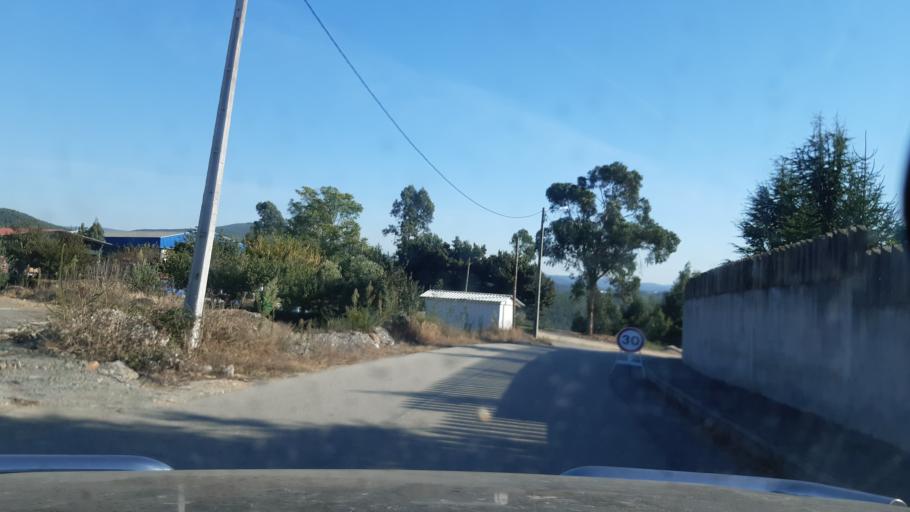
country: PT
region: Aveiro
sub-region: Agueda
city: Aguada de Cima
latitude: 40.5697
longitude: -8.3639
